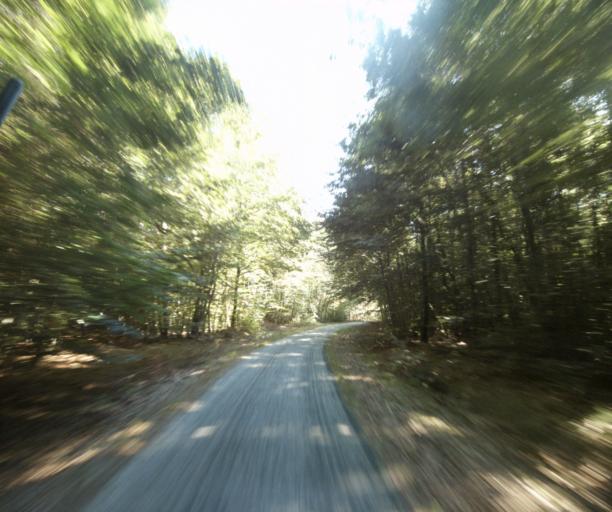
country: FR
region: Lorraine
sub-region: Departement des Vosges
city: Aydoilles
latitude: 48.1777
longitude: 6.5565
